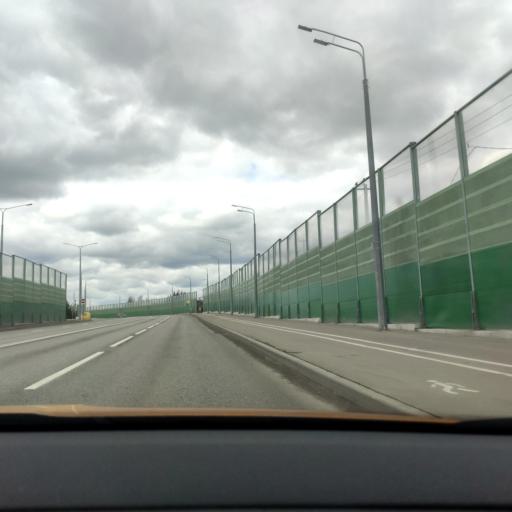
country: RU
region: Moskovskaya
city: Annino
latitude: 55.5301
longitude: 37.2348
